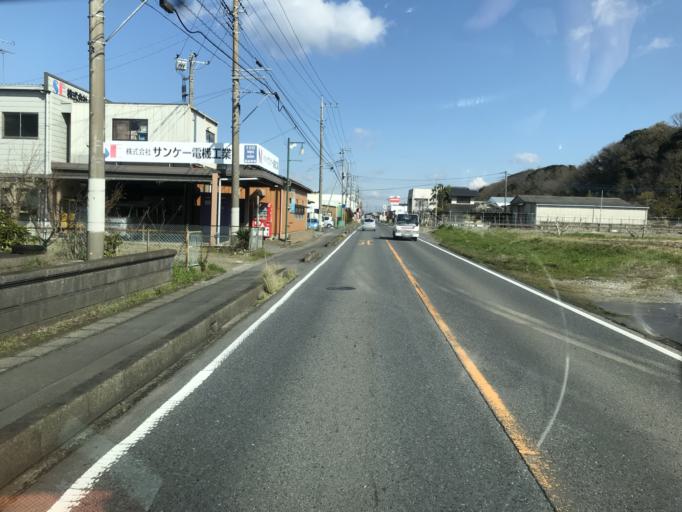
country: JP
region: Ibaraki
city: Itako
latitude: 35.9957
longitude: 140.4732
